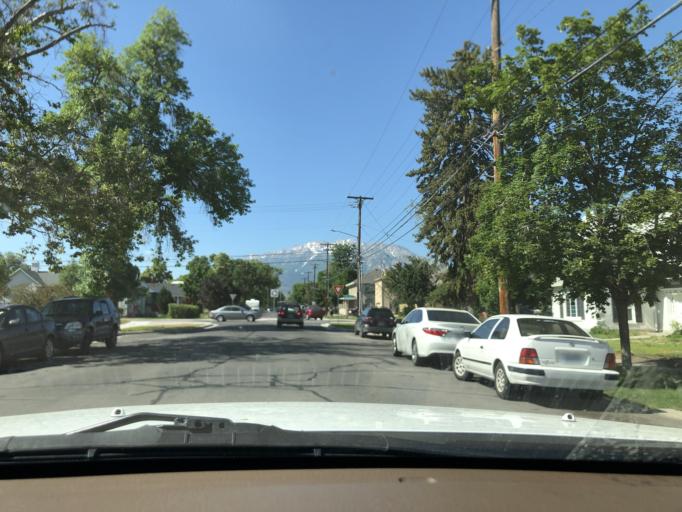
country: US
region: Utah
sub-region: Utah County
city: Provo
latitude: 40.2359
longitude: -111.6551
